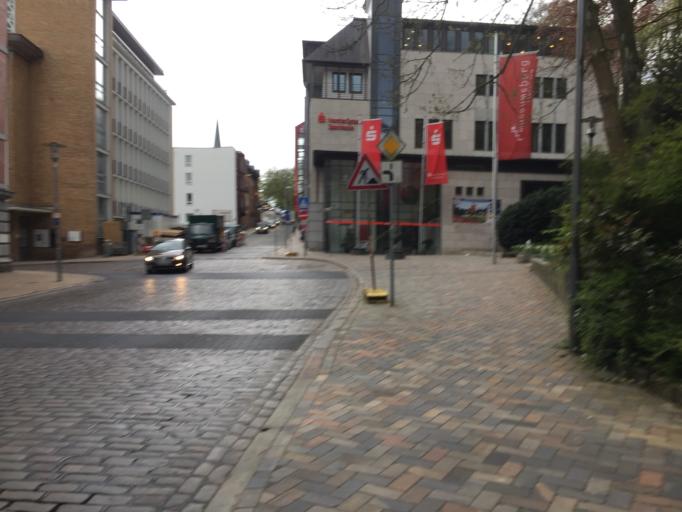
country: DE
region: Schleswig-Holstein
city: Flensburg
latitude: 54.7862
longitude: 9.4327
